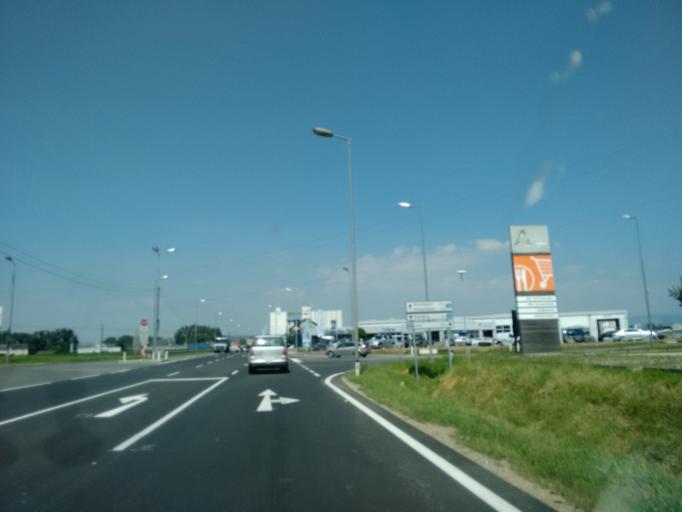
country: AT
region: Upper Austria
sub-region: Politischer Bezirk Urfahr-Umgebung
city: Feldkirchen an der Donau
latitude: 48.2969
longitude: 14.0114
